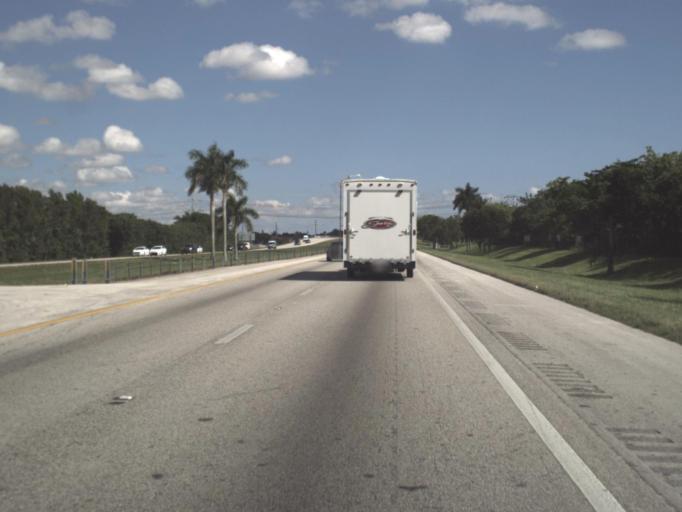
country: US
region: Florida
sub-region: Miami-Dade County
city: Princeton
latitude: 25.5215
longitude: -80.4015
